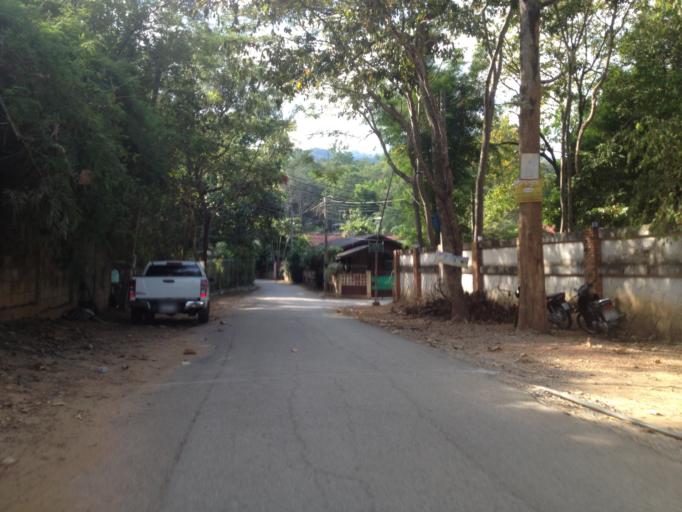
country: TH
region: Chiang Mai
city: Chiang Mai
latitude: 18.7856
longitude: 98.9517
